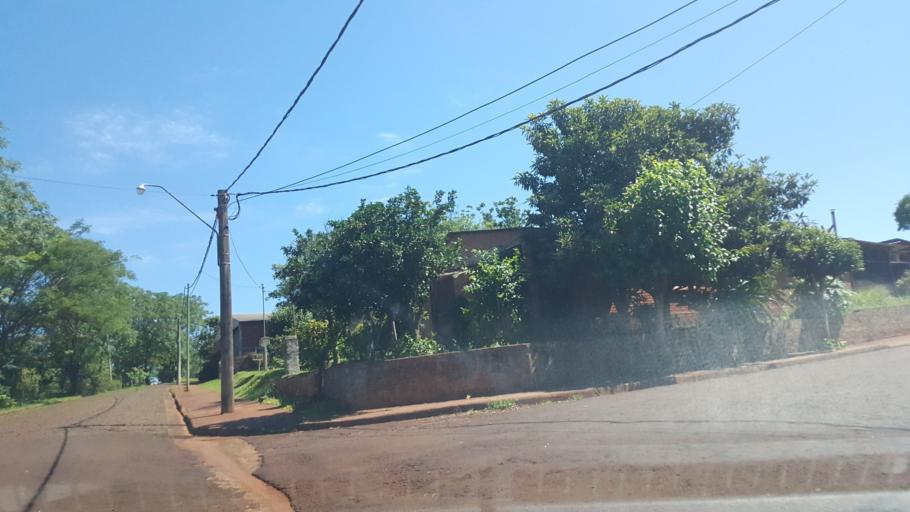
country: AR
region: Misiones
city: Capiovi
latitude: -26.9318
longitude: -55.0606
